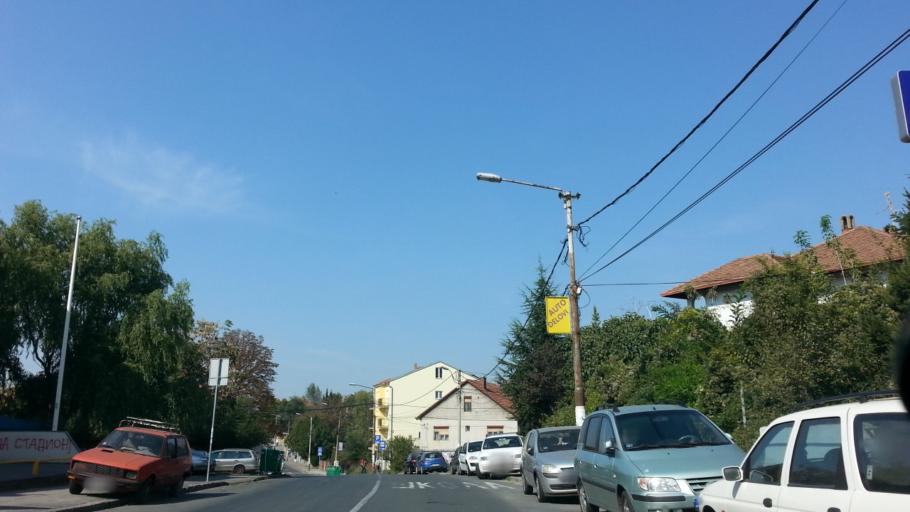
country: RS
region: Central Serbia
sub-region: Belgrade
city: Rakovica
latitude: 44.7560
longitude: 20.4212
